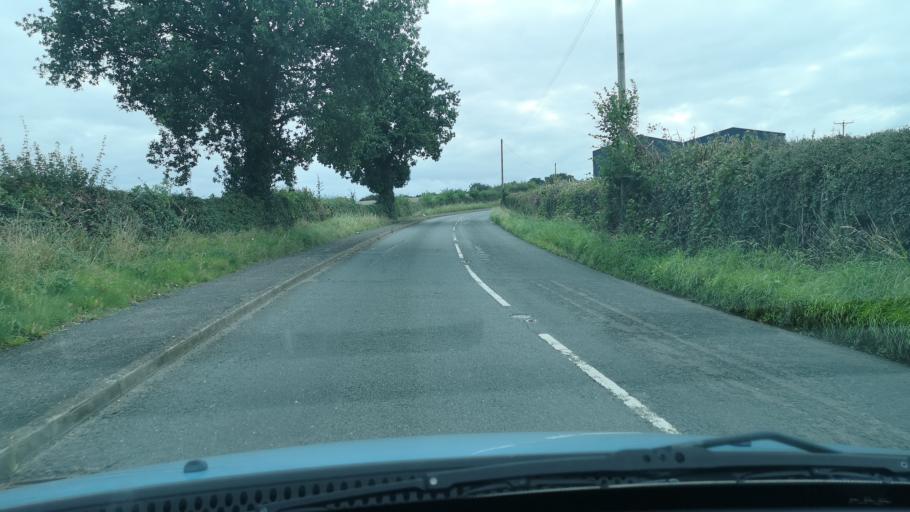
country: GB
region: England
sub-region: City and Borough of Wakefield
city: Crigglestone
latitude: 53.6336
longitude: -1.5462
